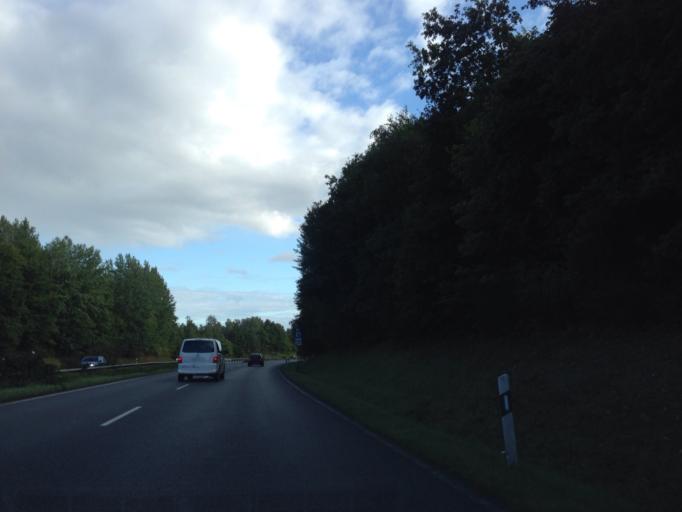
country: DE
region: Lower Saxony
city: Wendisch Evern
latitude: 53.2450
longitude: 10.4538
